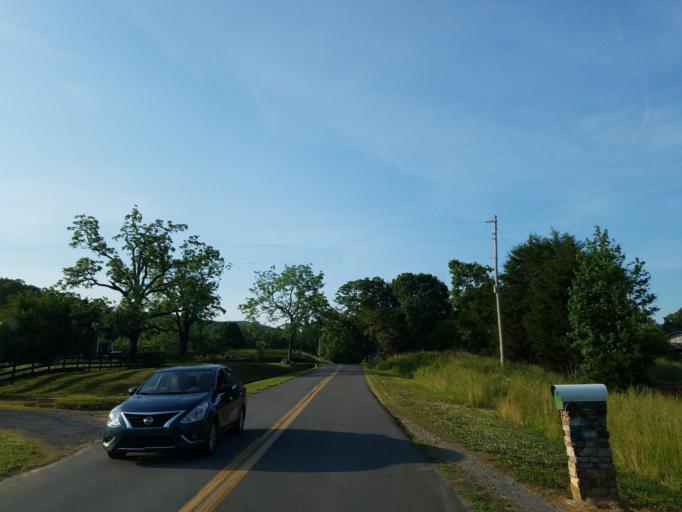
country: US
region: Georgia
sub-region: Gordon County
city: Calhoun
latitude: 34.5456
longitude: -85.1079
